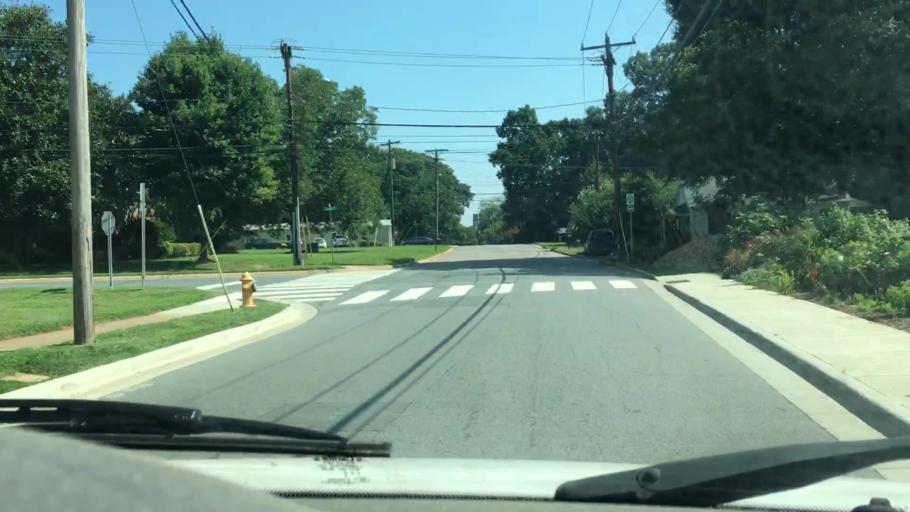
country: US
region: North Carolina
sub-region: Mecklenburg County
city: Cornelius
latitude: 35.4971
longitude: -80.8531
